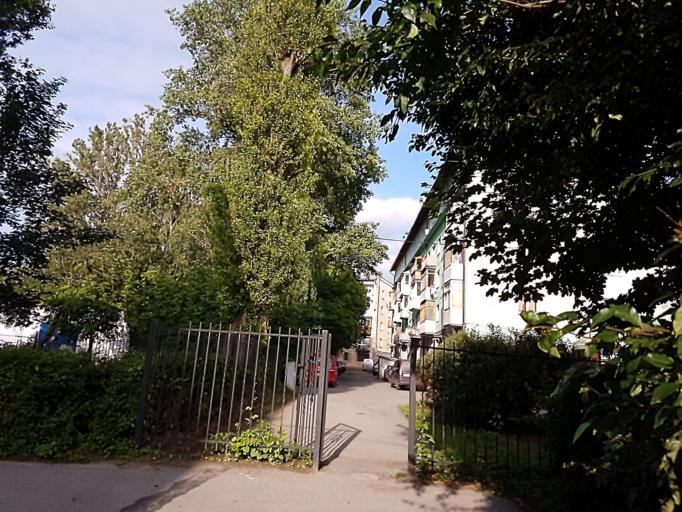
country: RU
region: Kaliningrad
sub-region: Gorod Kaliningrad
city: Kaliningrad
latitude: 54.6976
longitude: 20.5148
